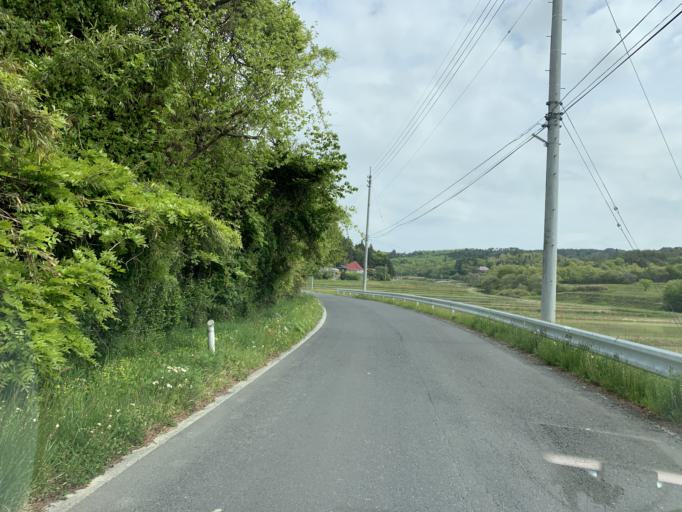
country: JP
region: Iwate
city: Ichinoseki
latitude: 38.8416
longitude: 141.1928
